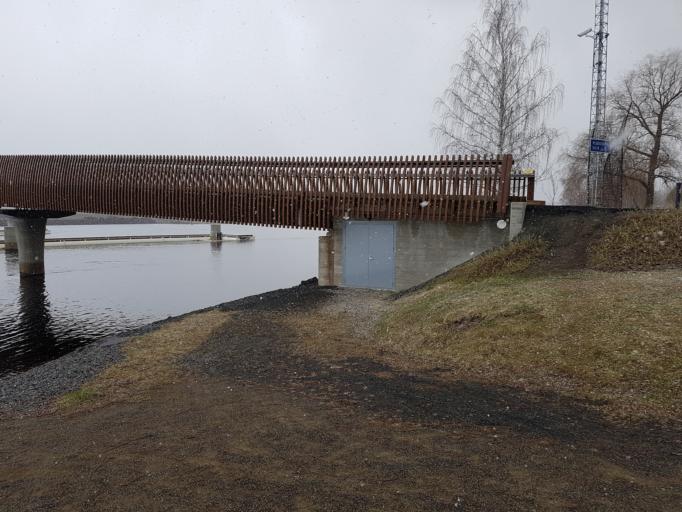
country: FI
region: North Karelia
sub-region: Joensuu
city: Joensuu
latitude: 62.5932
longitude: 29.7587
